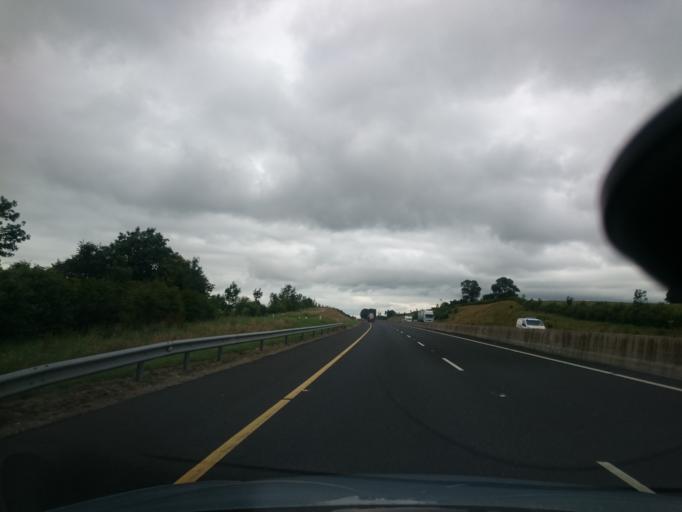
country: IE
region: Leinster
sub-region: Kildare
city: Old Kilcullen
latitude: 53.0444
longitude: -6.7916
